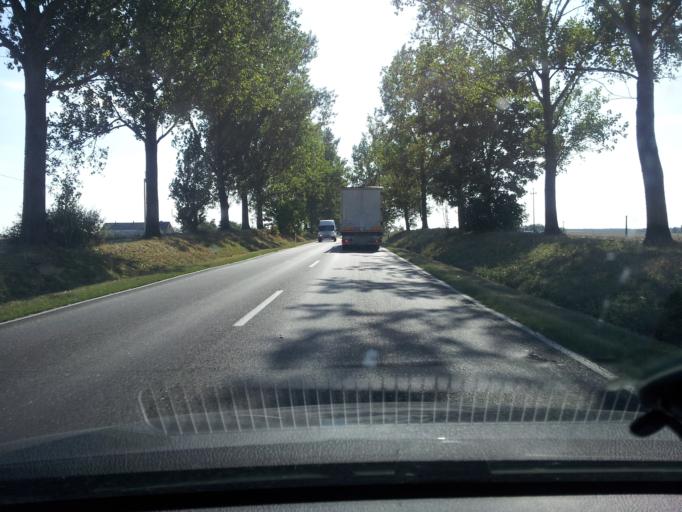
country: PL
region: Kujawsko-Pomorskie
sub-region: Powiat golubsko-dobrzynski
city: Kowalewo Pomorskie
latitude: 53.1299
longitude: 18.8437
